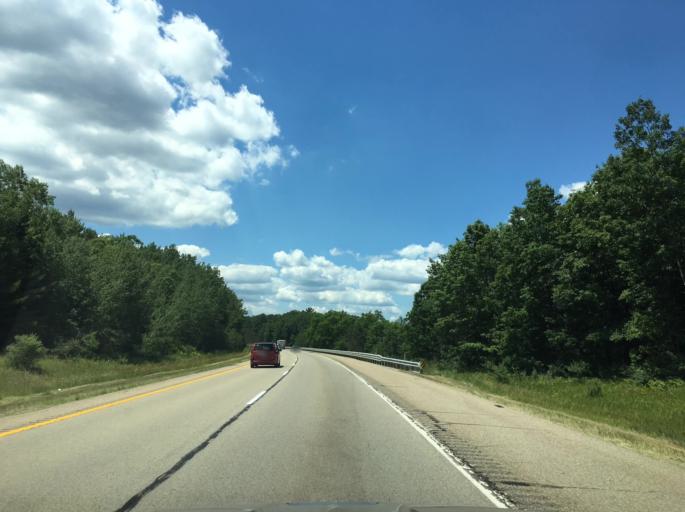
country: US
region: Michigan
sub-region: Clare County
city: Clare
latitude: 43.8836
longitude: -84.8077
